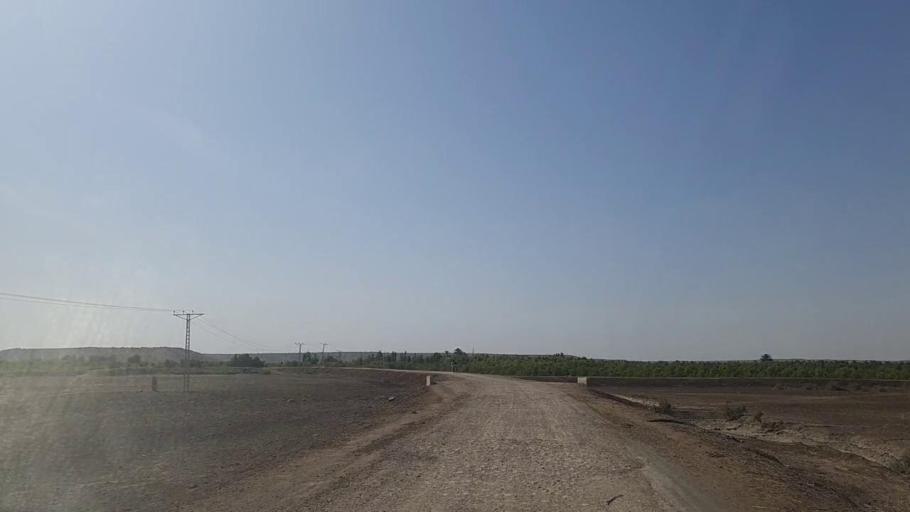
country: PK
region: Sindh
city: Thatta
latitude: 24.6403
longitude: 67.8825
